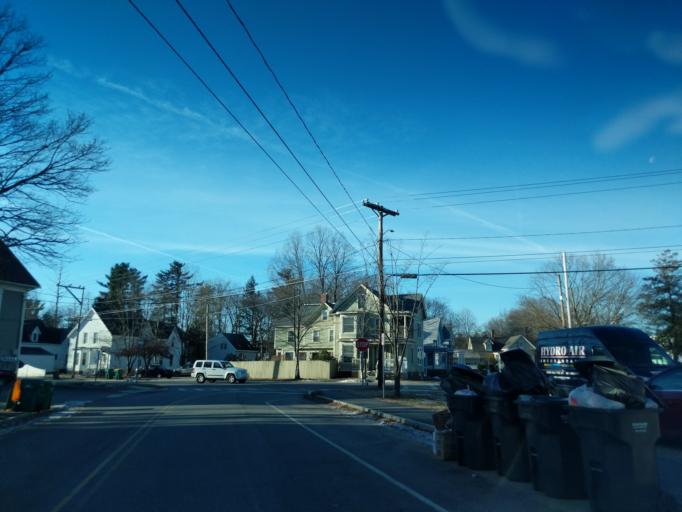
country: US
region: New Hampshire
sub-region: Strafford County
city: Rochester
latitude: 43.2989
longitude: -70.9743
